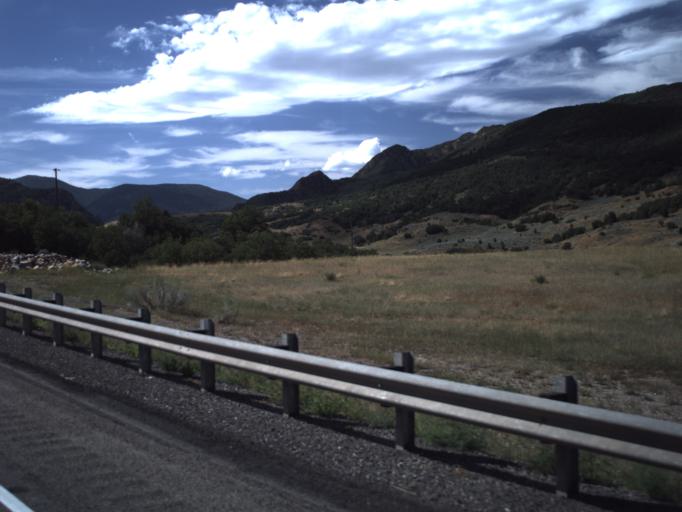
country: US
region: Utah
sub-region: Utah County
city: Mapleton
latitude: 40.0262
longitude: -111.5007
